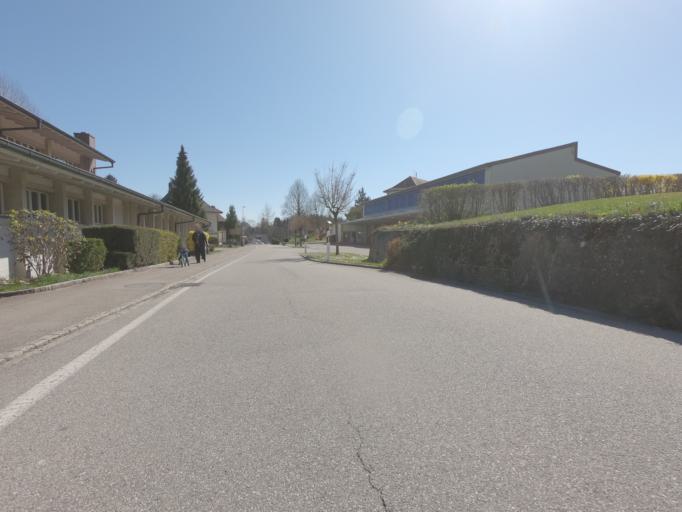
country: CH
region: Solothurn
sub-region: Bezirk Lebern
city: Riedholz
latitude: 47.2297
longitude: 7.5655
